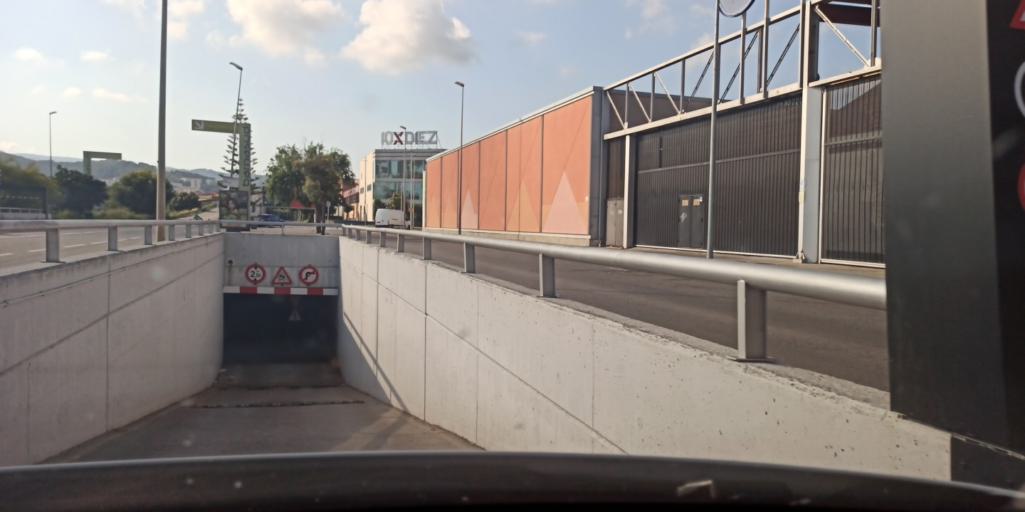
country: ES
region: Catalonia
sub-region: Provincia de Barcelona
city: Gava
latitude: 41.2951
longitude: 2.0068
